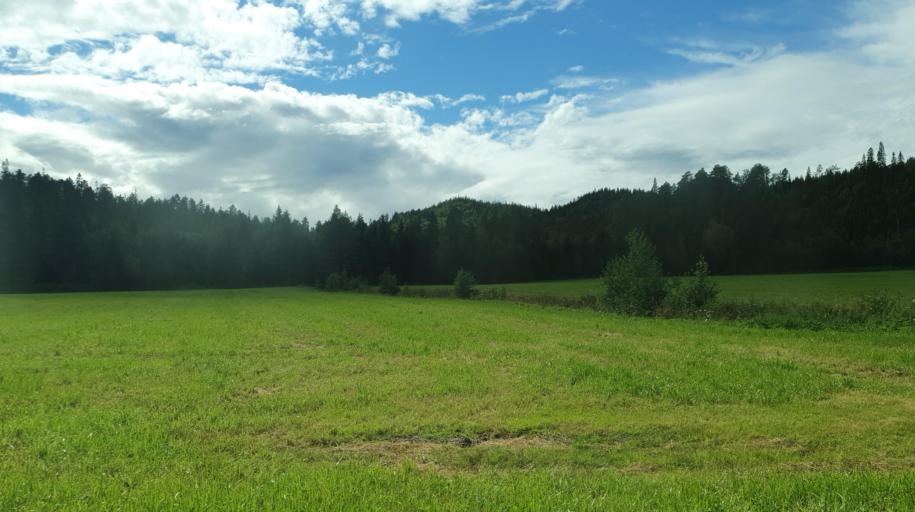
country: NO
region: Nord-Trondelag
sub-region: Levanger
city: Skogn
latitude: 63.5956
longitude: 11.2680
